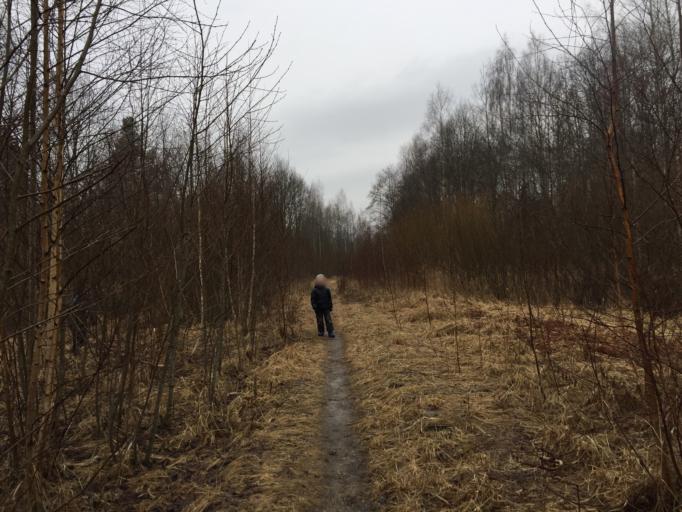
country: LV
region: Lielvarde
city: Lielvarde
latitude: 56.7267
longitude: 24.7795
